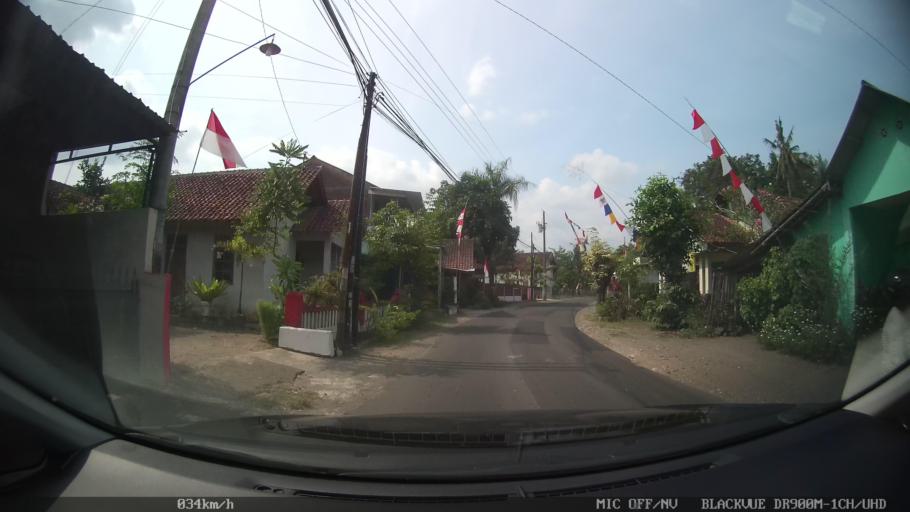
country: ID
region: Daerah Istimewa Yogyakarta
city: Depok
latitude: -7.7891
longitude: 110.4473
